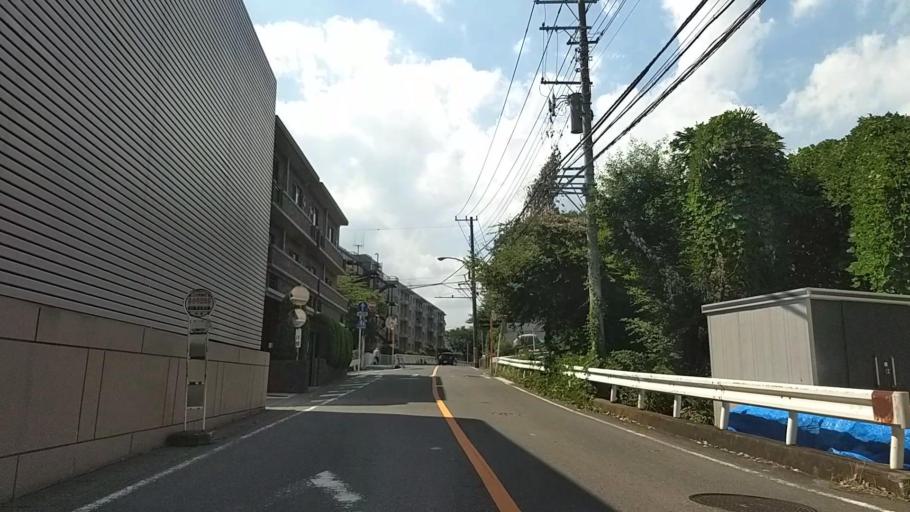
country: JP
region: Kanagawa
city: Yokohama
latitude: 35.5084
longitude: 139.5887
